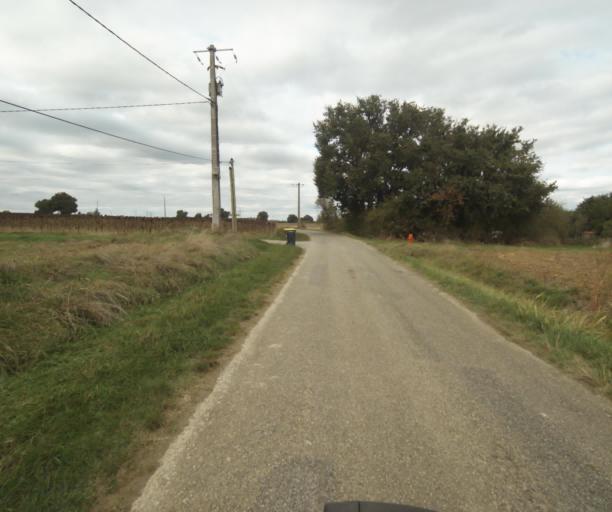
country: FR
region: Midi-Pyrenees
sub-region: Departement du Tarn-et-Garonne
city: Verdun-sur-Garonne
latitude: 43.8688
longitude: 1.1696
